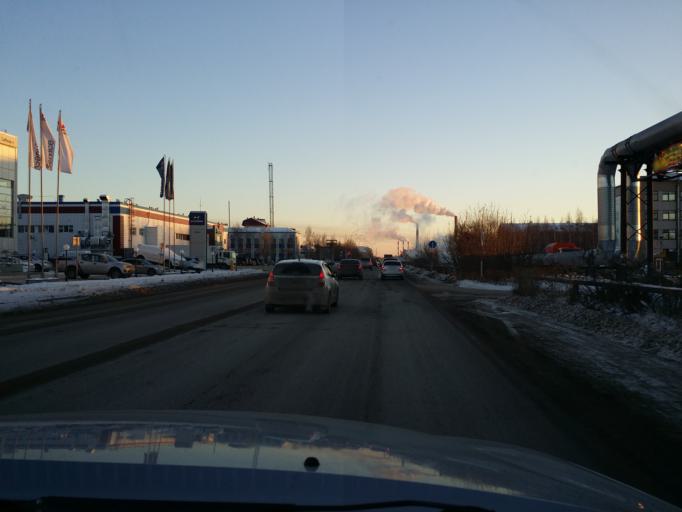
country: RU
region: Khanty-Mansiyskiy Avtonomnyy Okrug
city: Nizhnevartovsk
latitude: 60.9468
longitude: 76.5480
